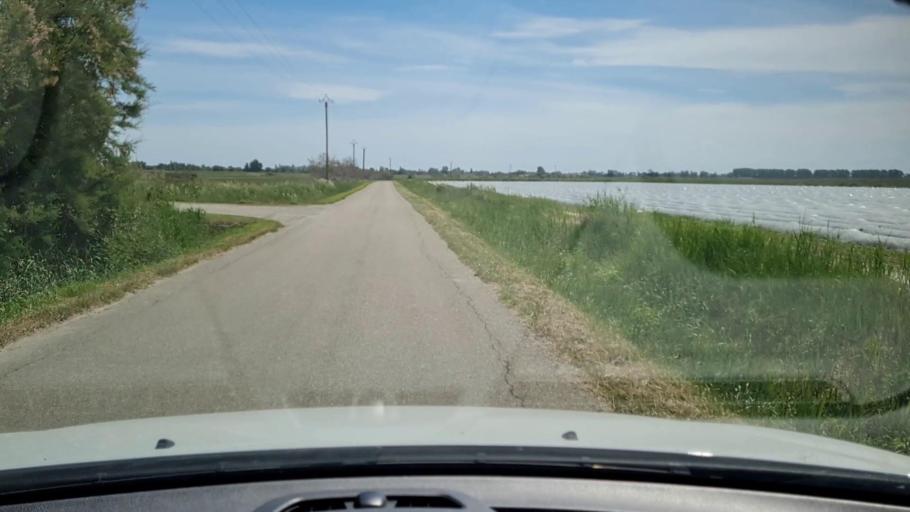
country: FR
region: Languedoc-Roussillon
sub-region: Departement du Gard
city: Saint-Gilles
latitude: 43.5986
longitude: 4.4595
